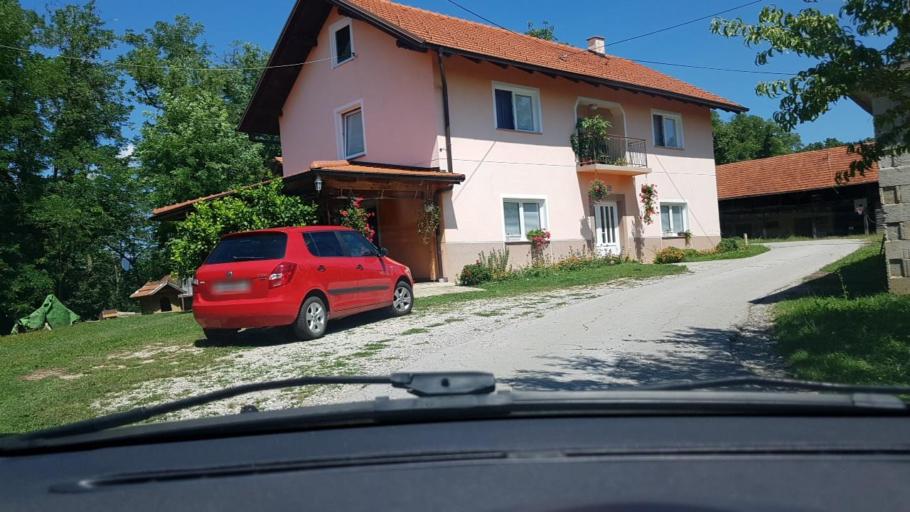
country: HR
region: Krapinsko-Zagorska
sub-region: Grad Krapina
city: Krapina
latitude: 46.1124
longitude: 15.8531
